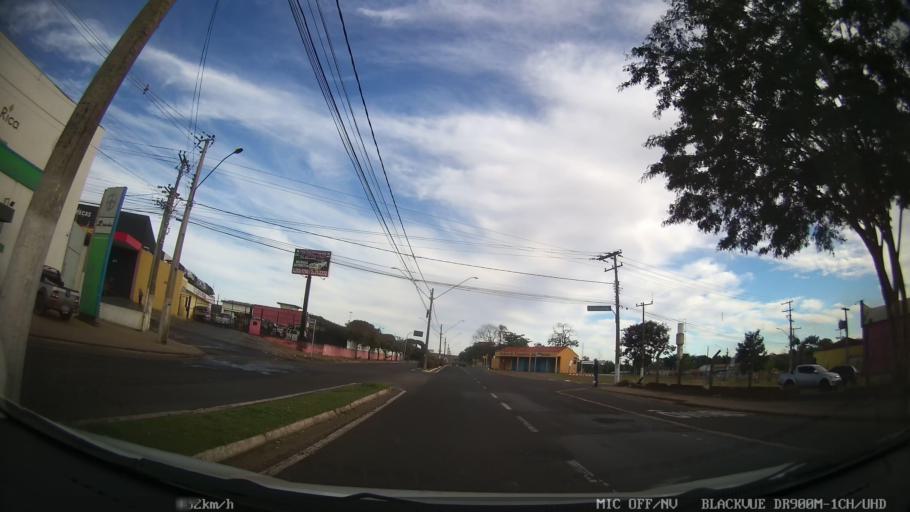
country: BR
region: Sao Paulo
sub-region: Catanduva
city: Catanduva
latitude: -21.1248
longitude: -48.9859
